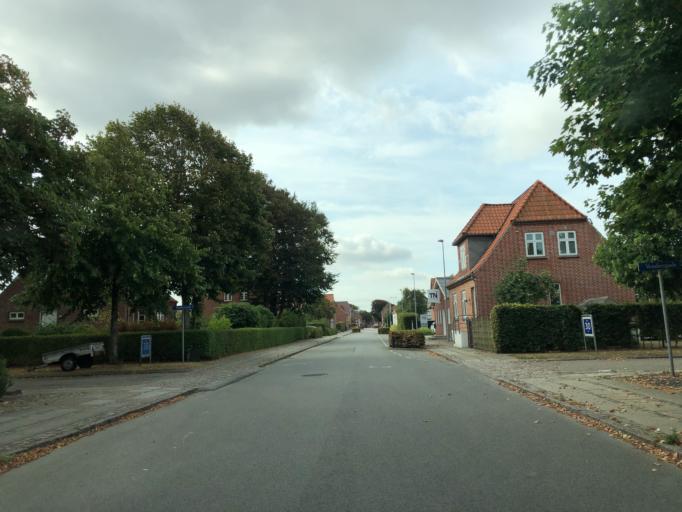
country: DK
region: Central Jutland
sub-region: Ringkobing-Skjern Kommune
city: Skjern
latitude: 55.9518
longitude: 8.4930
